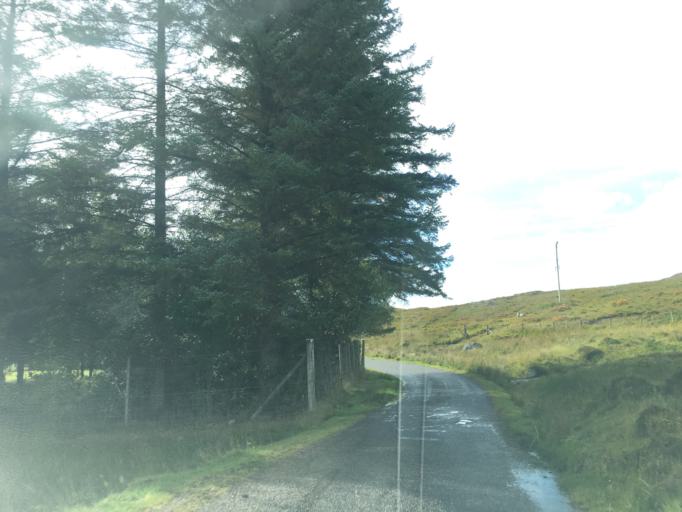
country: GB
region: Scotland
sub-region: Highland
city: Spean Bridge
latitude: 57.3420
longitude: -4.9435
